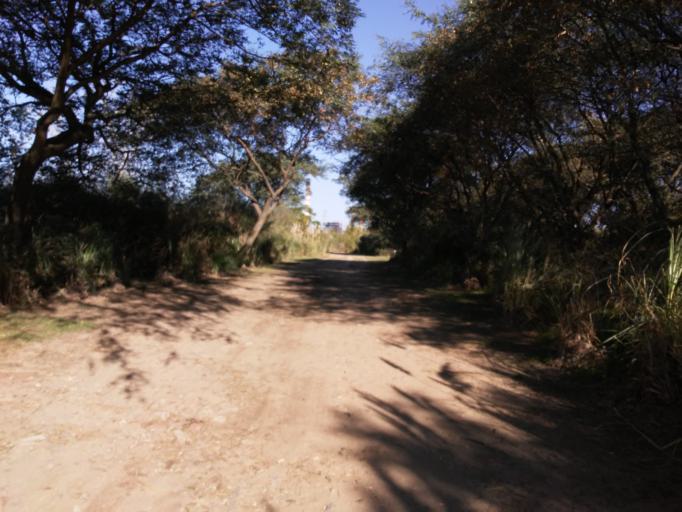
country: AR
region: Buenos Aires F.D.
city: Buenos Aires
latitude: -34.6147
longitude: -58.3402
